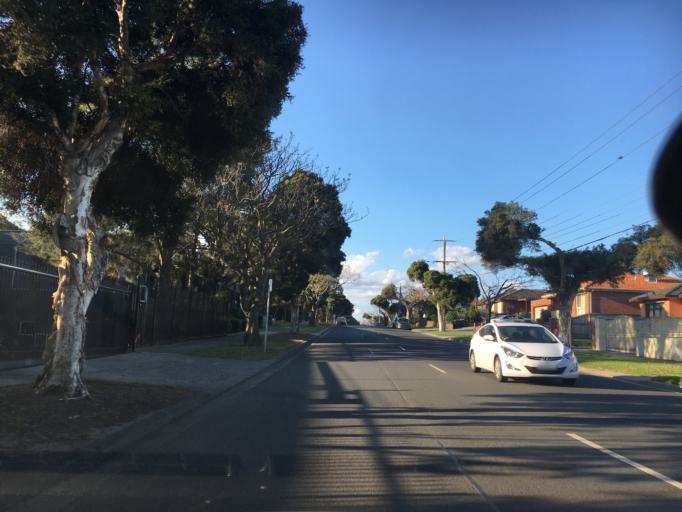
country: AU
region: Victoria
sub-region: Kingston
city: Clayton South
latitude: -37.9379
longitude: 145.1268
